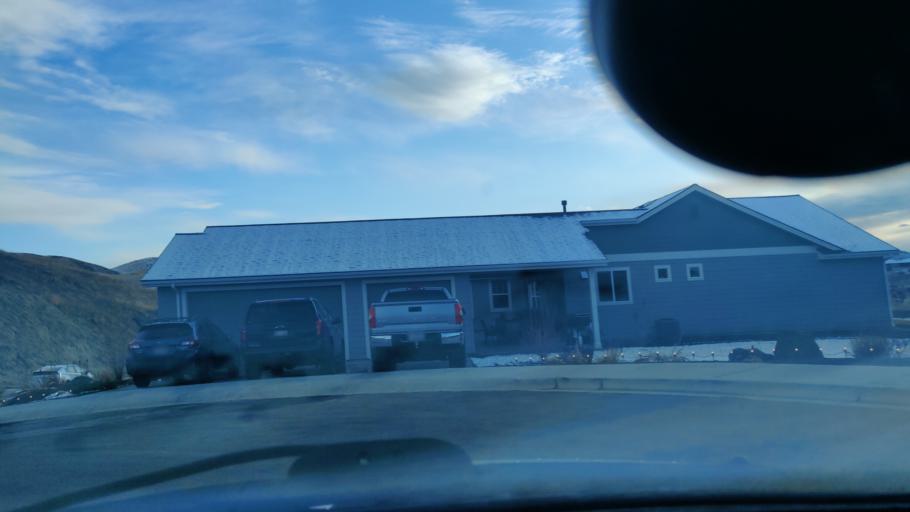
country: US
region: Idaho
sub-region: Ada County
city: Eagle
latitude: 43.7750
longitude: -116.2514
